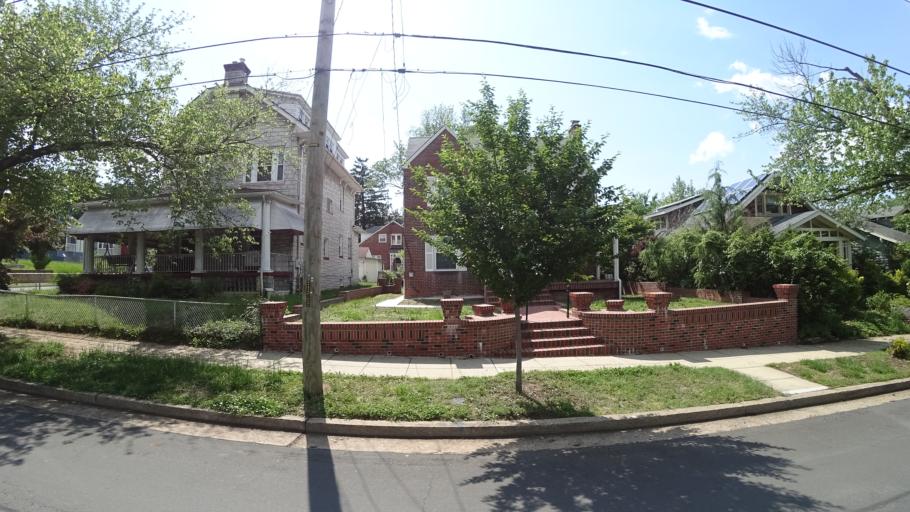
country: US
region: Maryland
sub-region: Prince George's County
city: Mount Rainier
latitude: 38.9313
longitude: -76.9763
